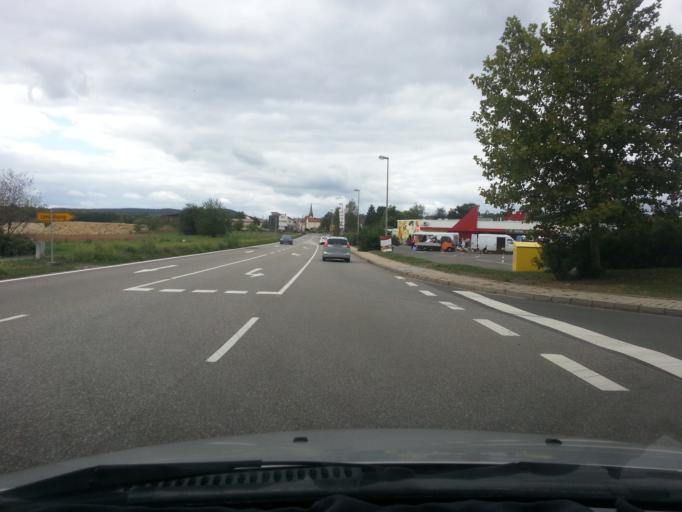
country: DE
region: Rheinland-Pfalz
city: Eisenberg
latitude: 49.5629
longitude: 8.0855
